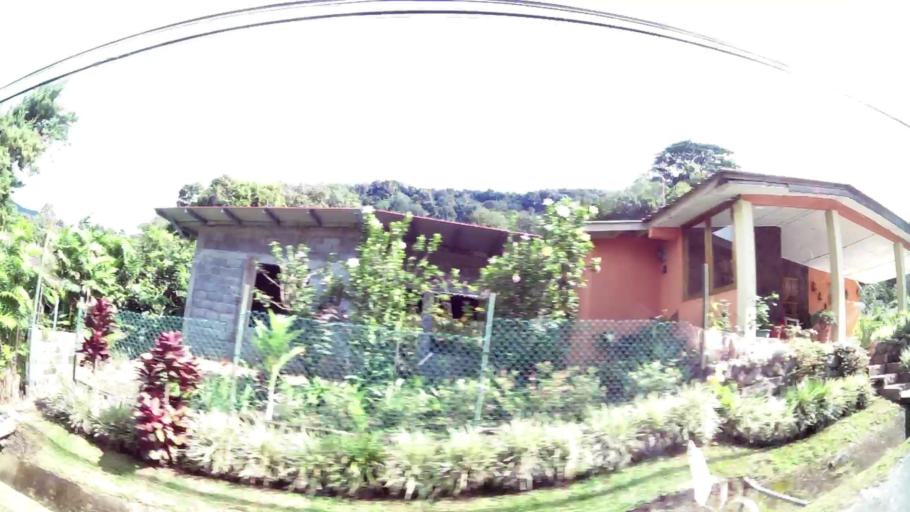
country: PA
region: Chiriqui
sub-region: Distrito Boquete
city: Boquete
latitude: 8.7882
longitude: -82.4233
